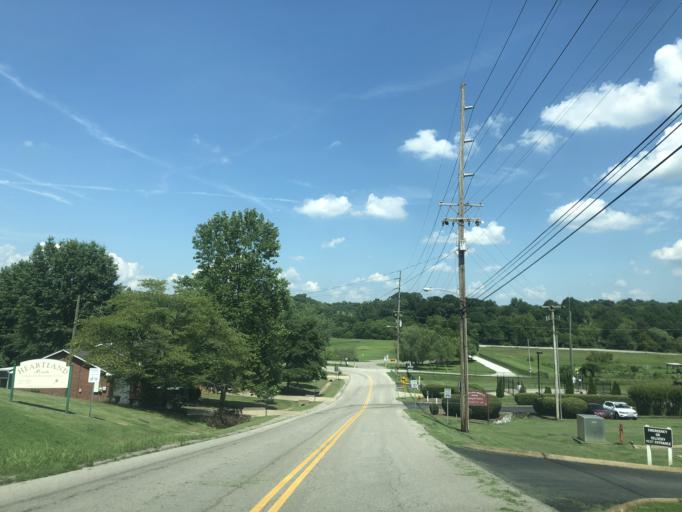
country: US
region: Tennessee
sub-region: Davidson County
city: Lakewood
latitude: 36.1853
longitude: -86.6693
